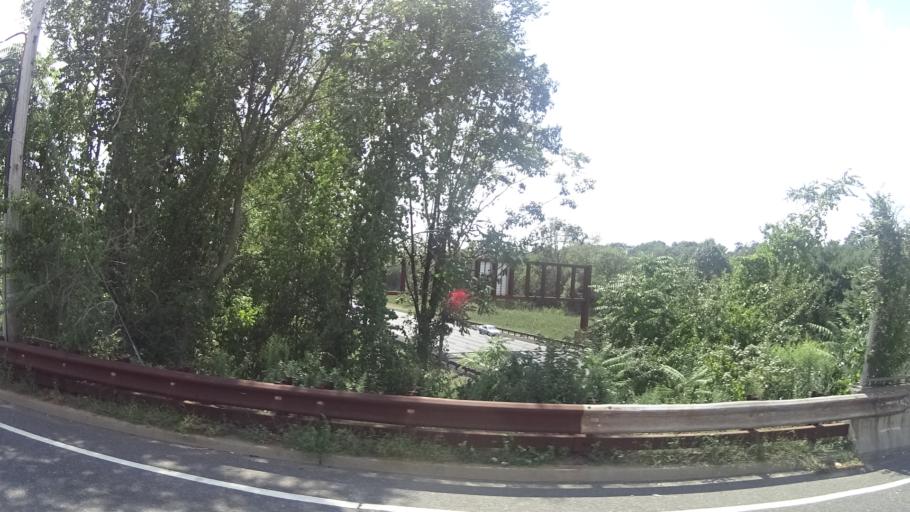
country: US
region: New Jersey
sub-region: Monmouth County
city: Ramtown
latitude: 40.1487
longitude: -74.1061
